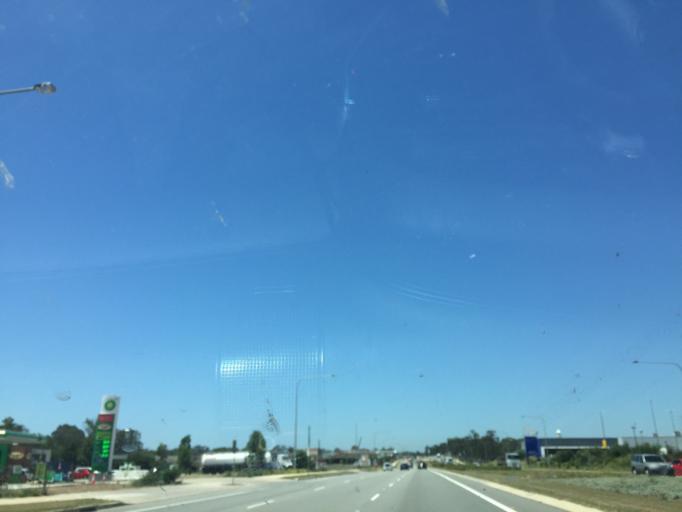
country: AU
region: New South Wales
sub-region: Blacktown
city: Hassall Grove
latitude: -33.7190
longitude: 150.8443
